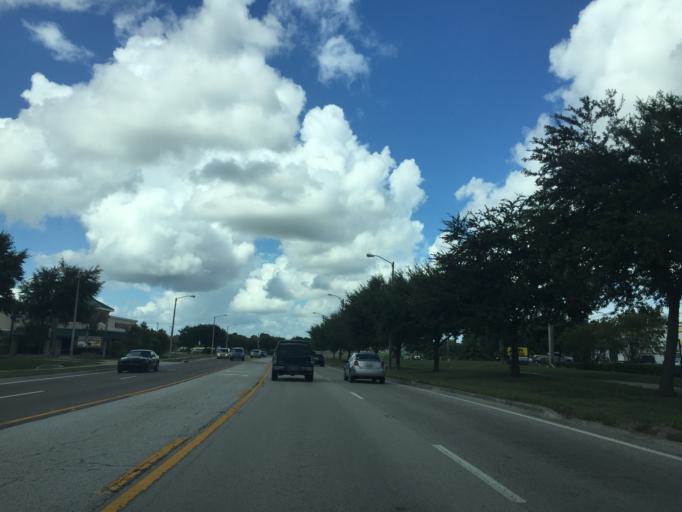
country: US
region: Florida
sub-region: Seminole County
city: Oviedo
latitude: 28.6557
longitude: -81.2131
